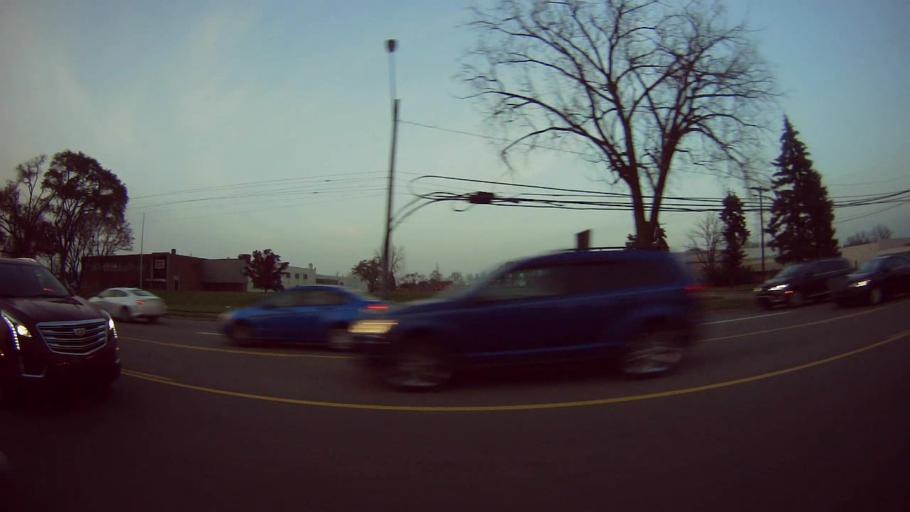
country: US
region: Michigan
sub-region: Oakland County
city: Madison Heights
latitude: 42.5047
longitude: -83.1045
